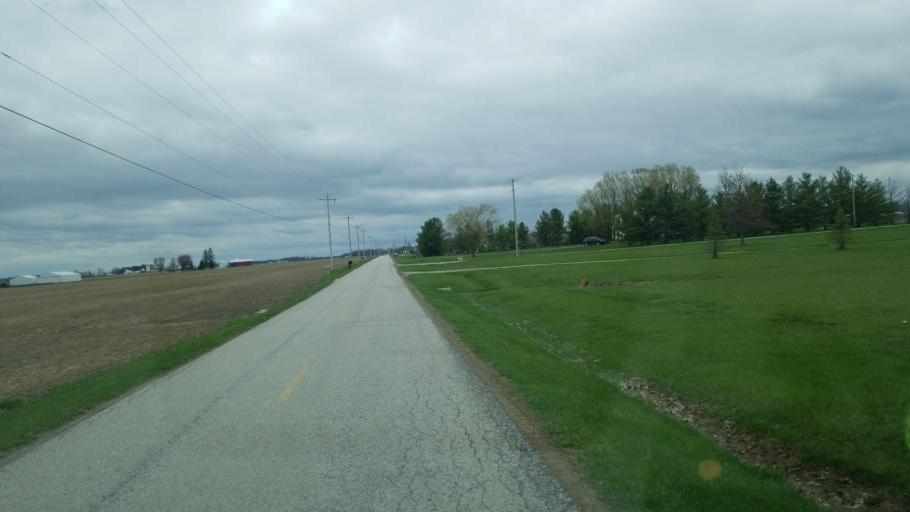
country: US
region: Ohio
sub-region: Marion County
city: Prospect
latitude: 40.3822
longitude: -83.1190
